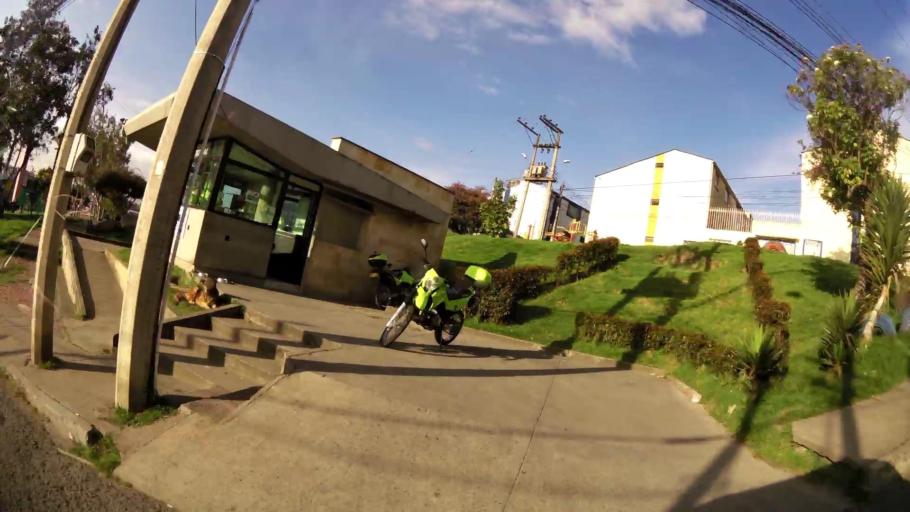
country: CO
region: Bogota D.C.
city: Bogota
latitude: 4.5442
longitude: -74.0956
